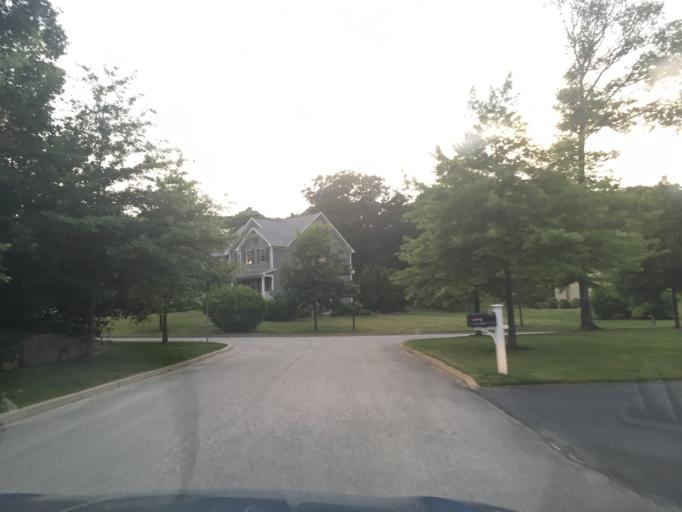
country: US
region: Rhode Island
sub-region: Washington County
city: Exeter
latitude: 41.6271
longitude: -71.5144
